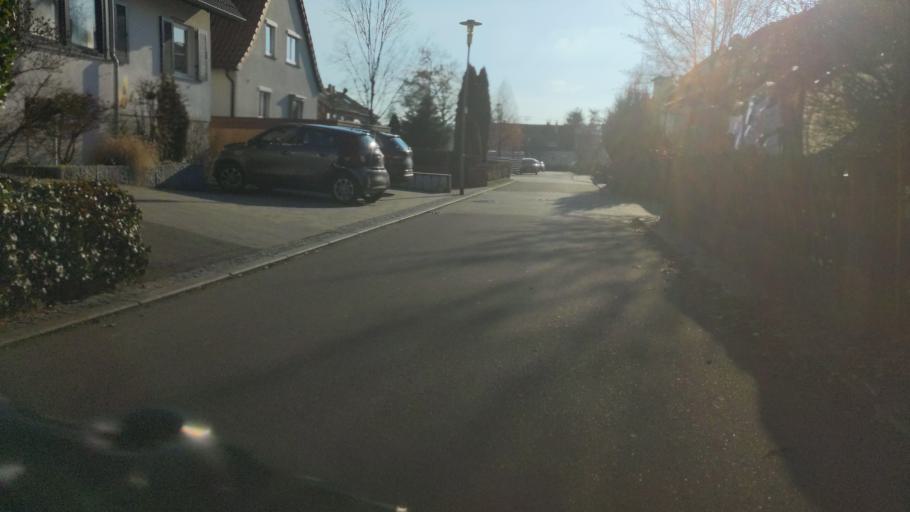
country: DE
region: Baden-Wuerttemberg
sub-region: Regierungsbezirk Stuttgart
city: Renningen
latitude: 48.7742
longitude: 8.9348
